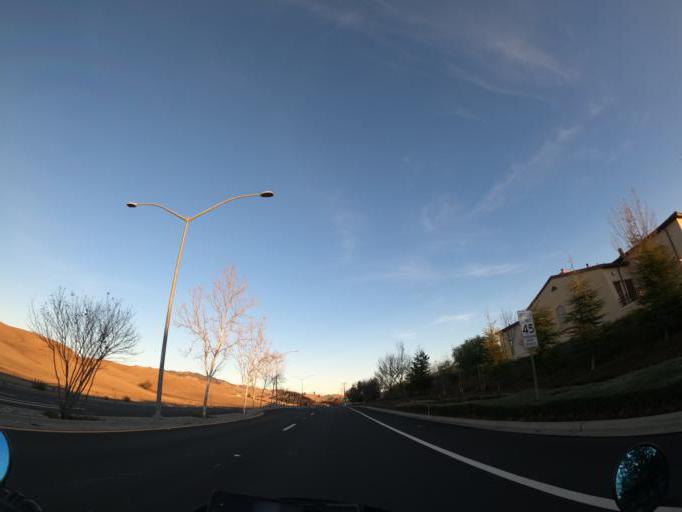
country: US
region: California
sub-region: Contra Costa County
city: Blackhawk
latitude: 37.7990
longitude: -121.8771
